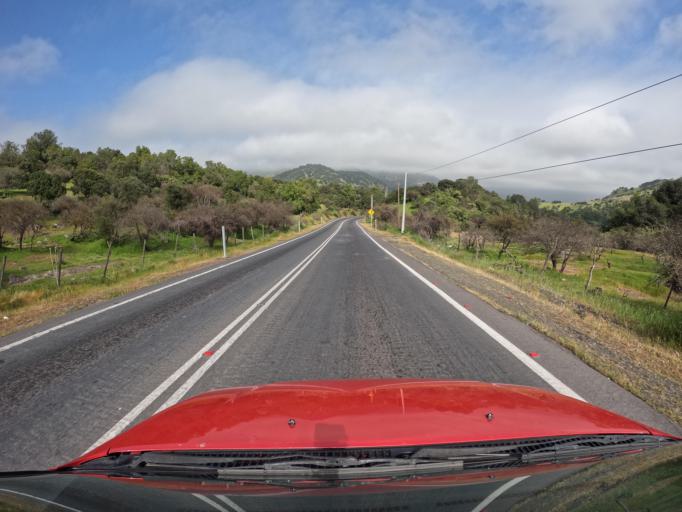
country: CL
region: Maule
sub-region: Provincia de Curico
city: Teno
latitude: -34.8177
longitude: -71.1991
